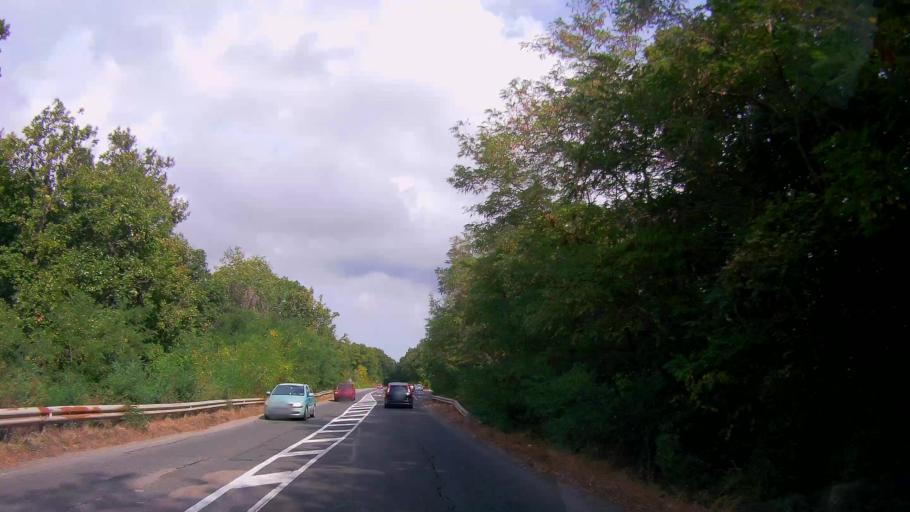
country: BG
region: Burgas
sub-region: Obshtina Primorsko
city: Primorsko
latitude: 42.2748
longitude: 27.7408
